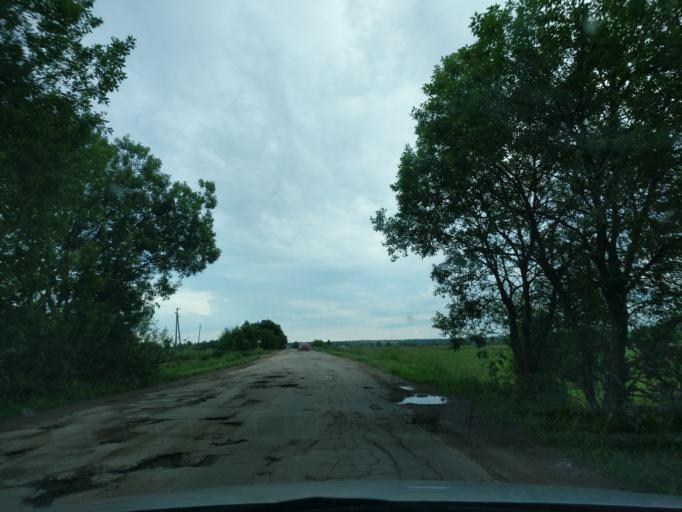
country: RU
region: Kaluga
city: Myatlevo
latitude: 54.7867
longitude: 35.7336
